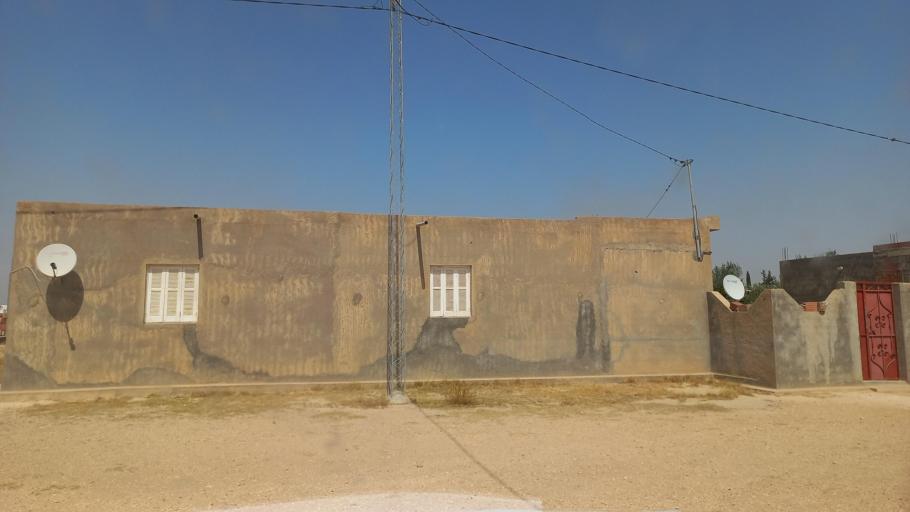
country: TN
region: Al Qasrayn
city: Kasserine
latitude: 35.2506
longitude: 9.0226
